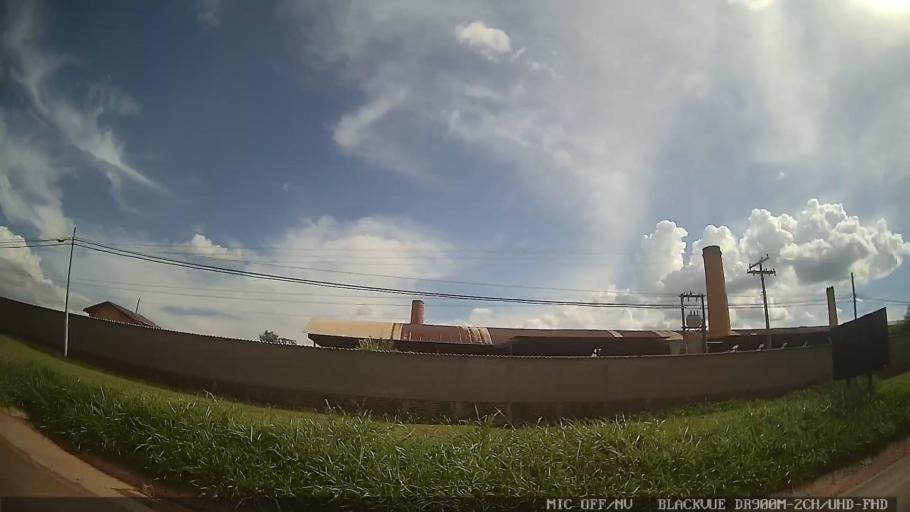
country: BR
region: Sao Paulo
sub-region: Laranjal Paulista
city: Laranjal Paulista
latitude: -23.0377
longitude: -47.8653
